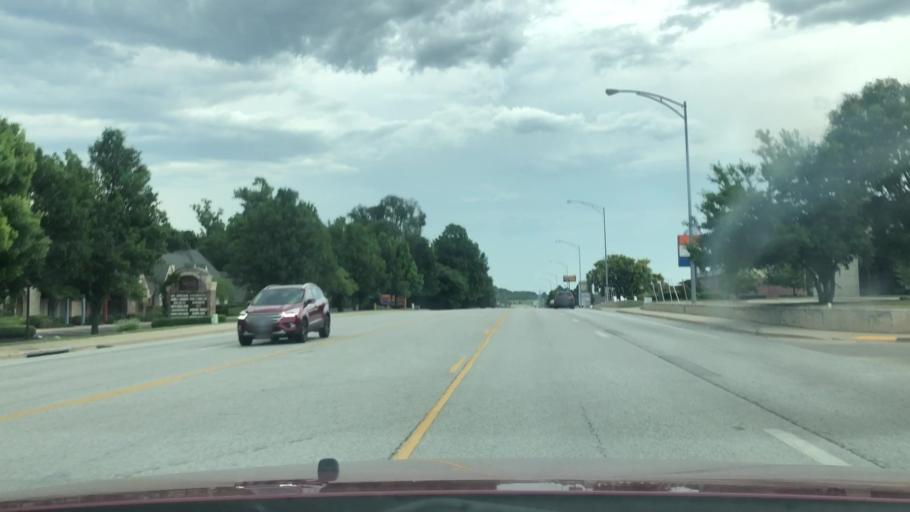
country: US
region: Missouri
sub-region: Greene County
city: Springfield
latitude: 37.1374
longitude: -93.2689
